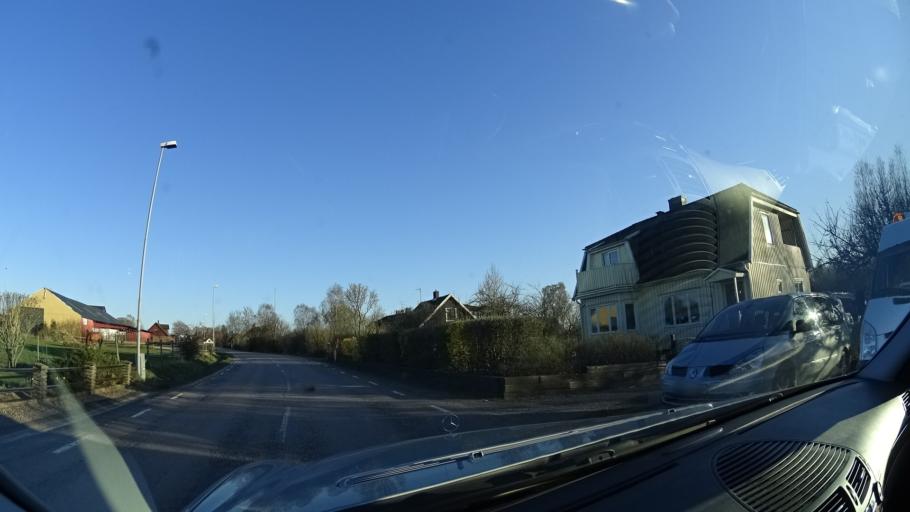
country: SE
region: Skane
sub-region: Bjuvs Kommun
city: Billesholm
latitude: 56.0517
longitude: 12.9982
